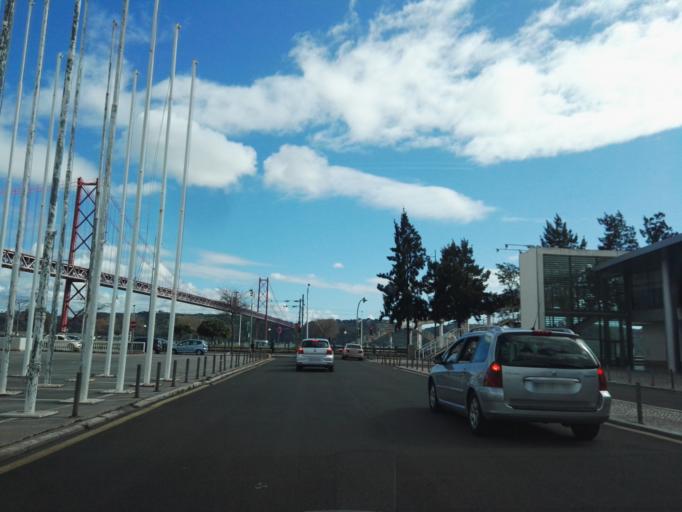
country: PT
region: Setubal
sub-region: Almada
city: Pragal
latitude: 38.6991
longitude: -9.1833
